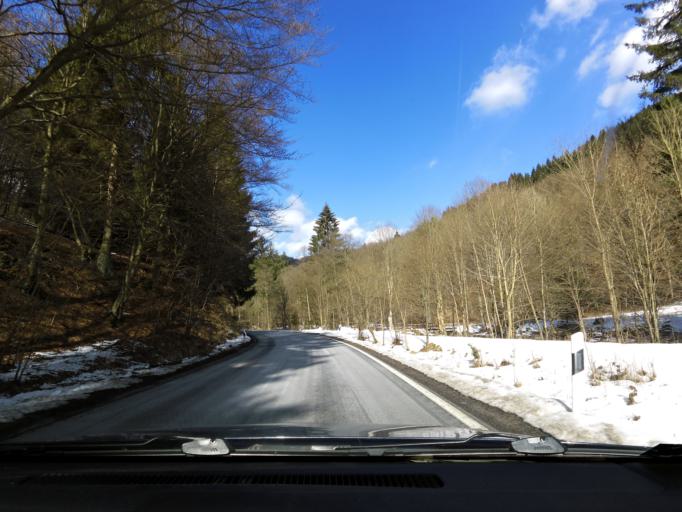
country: DE
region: Lower Saxony
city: Sankt Andreasberg
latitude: 51.6699
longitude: 10.5063
